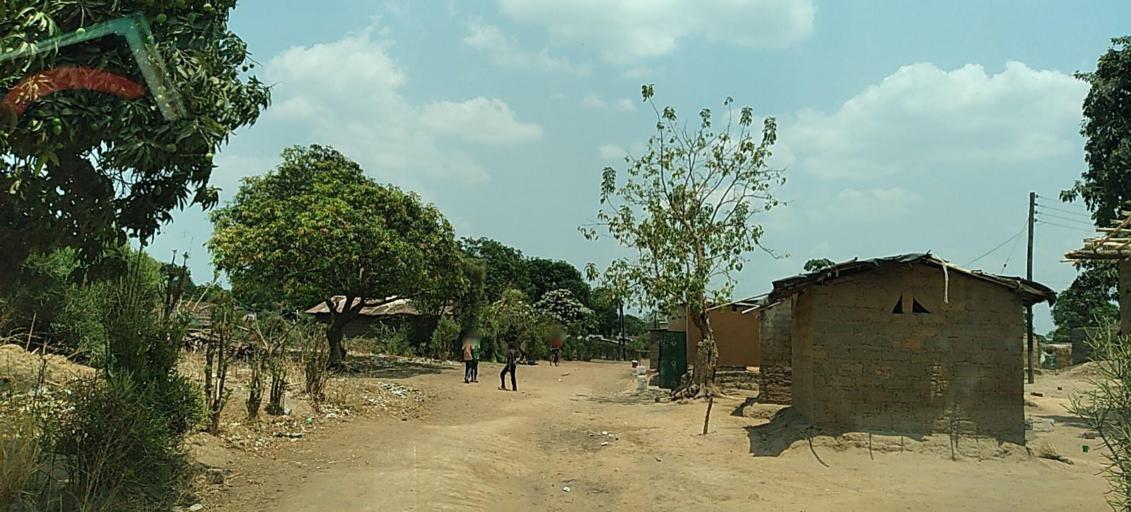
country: ZM
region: Copperbelt
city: Luanshya
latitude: -13.1203
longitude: 28.3084
